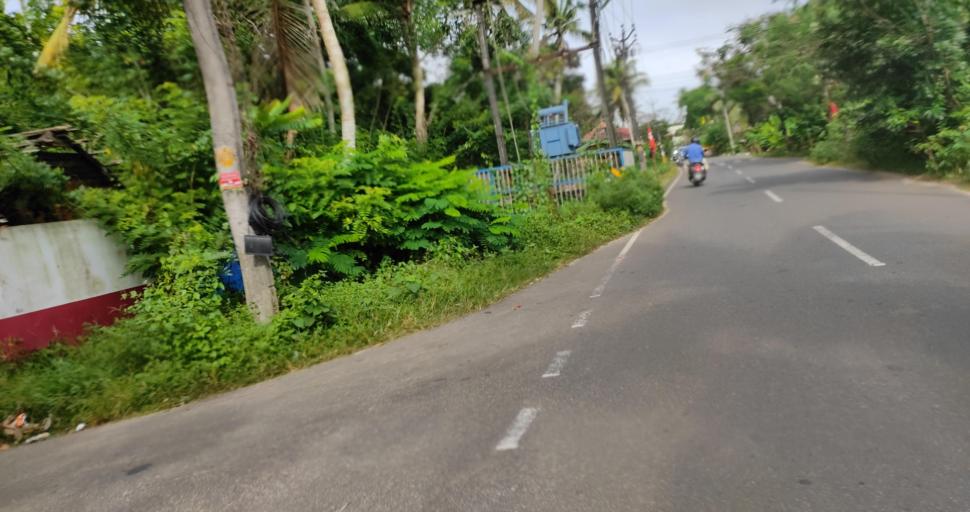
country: IN
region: Kerala
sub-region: Alappuzha
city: Vayalar
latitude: 9.6550
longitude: 76.3057
